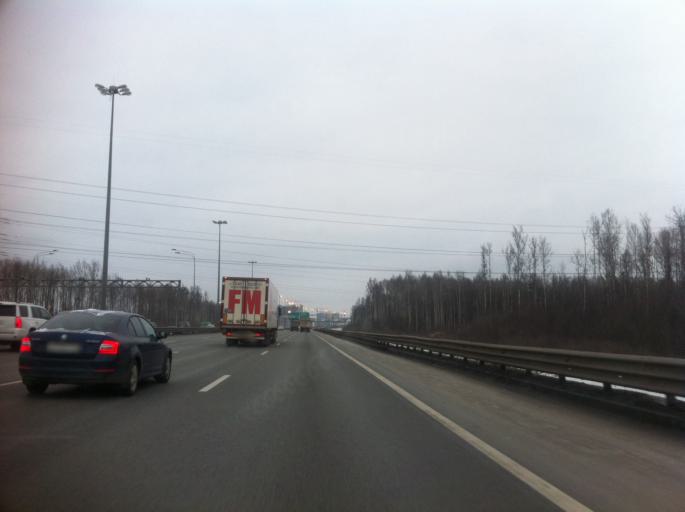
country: RU
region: Leningrad
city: Rybatskoye
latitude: 59.8755
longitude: 30.5311
